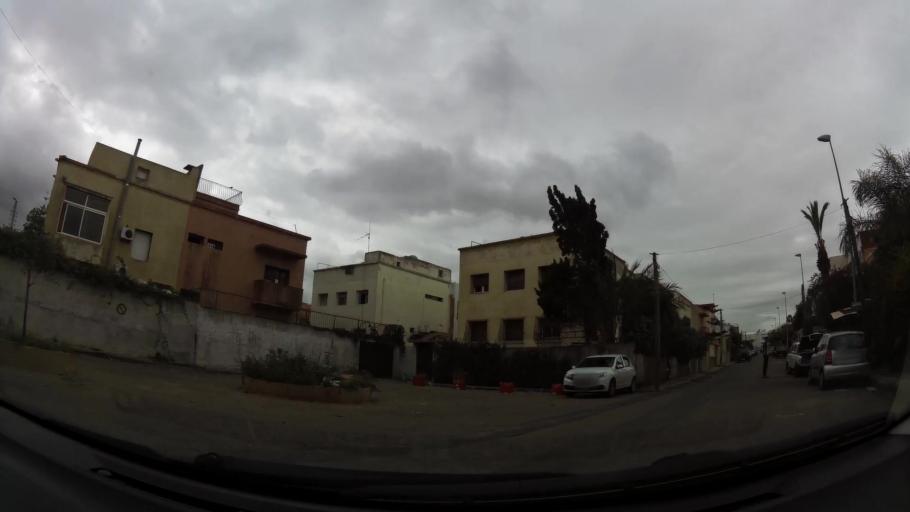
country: MA
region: Grand Casablanca
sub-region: Casablanca
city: Casablanca
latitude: 33.5740
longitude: -7.6656
